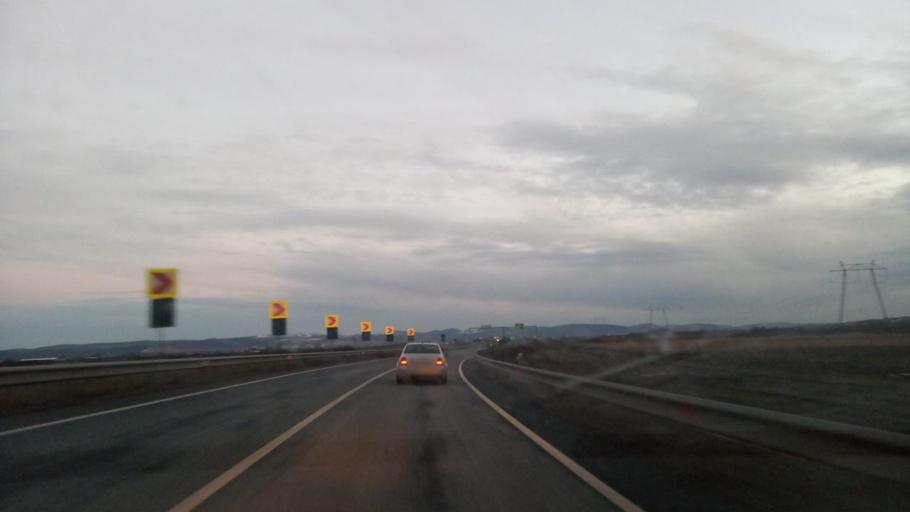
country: RO
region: Bacau
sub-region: Comuna Saucesti
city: Saucesti
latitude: 46.6371
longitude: 26.9320
